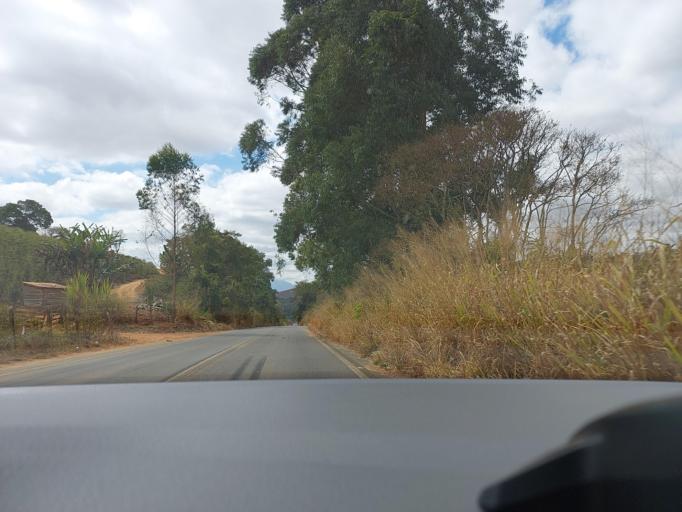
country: BR
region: Minas Gerais
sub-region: Vicosa
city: Vicosa
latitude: -20.8395
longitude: -42.7029
